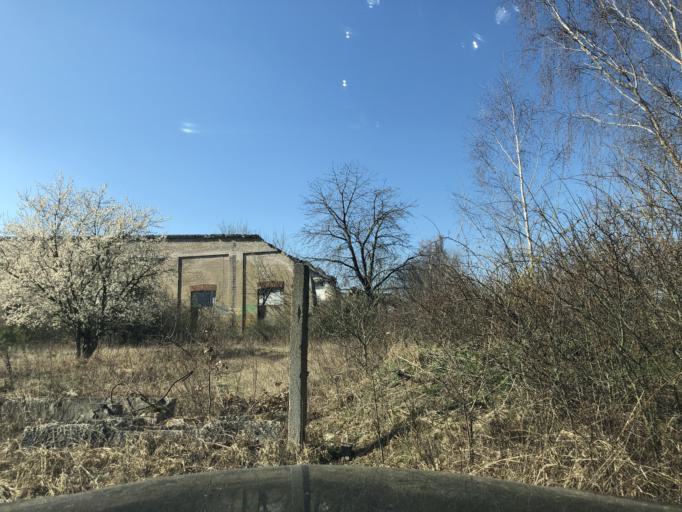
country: DE
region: Brandenburg
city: Ziesar
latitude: 52.2753
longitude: 12.3288
